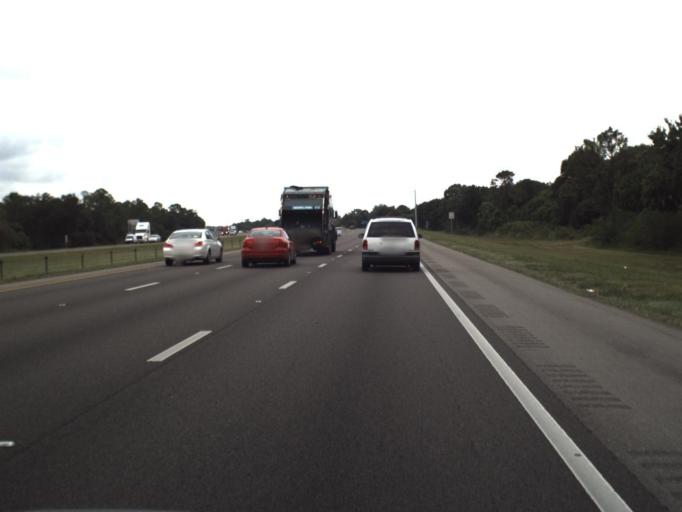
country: US
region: Florida
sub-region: Sarasota County
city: Desoto Lakes
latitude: 27.4316
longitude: -82.4598
